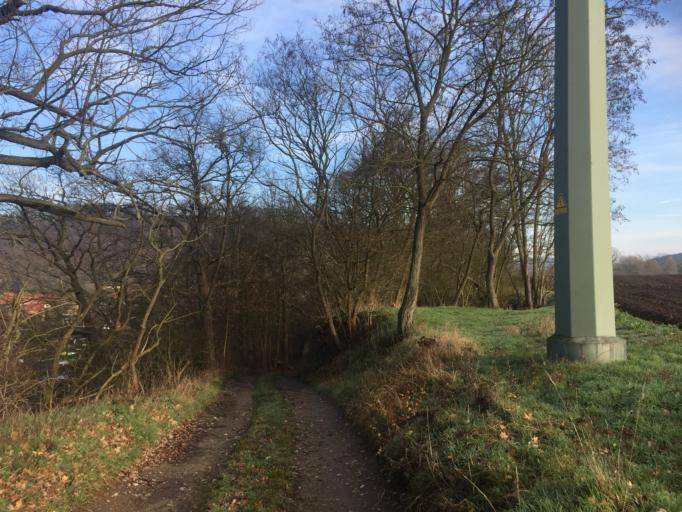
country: DE
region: Thuringia
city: Orlamunde
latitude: 50.7712
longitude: 11.5322
